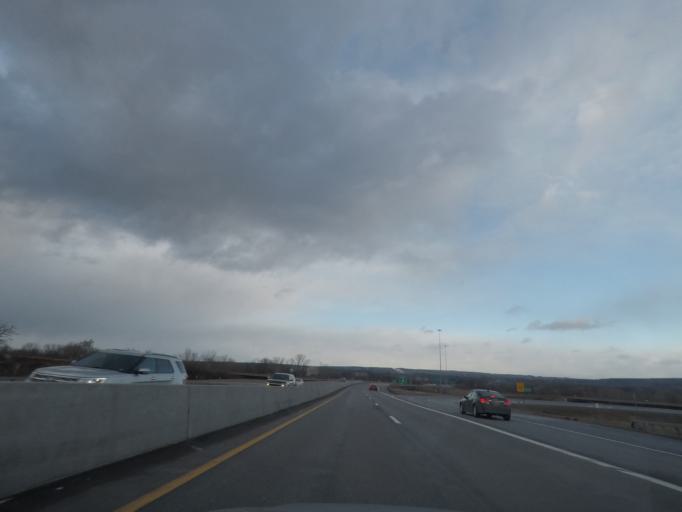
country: US
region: New York
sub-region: Oneida County
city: Utica
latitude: 43.1063
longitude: -75.2390
